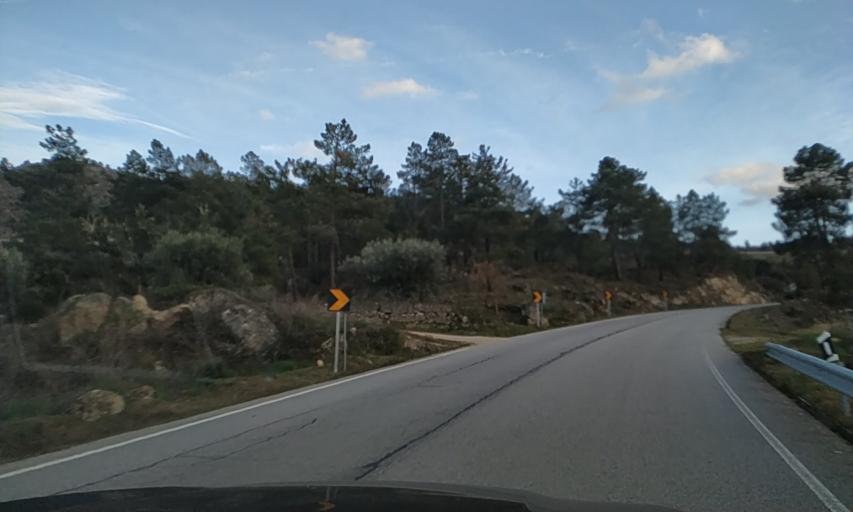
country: PT
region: Braganca
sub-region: Carrazeda de Ansiaes
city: Carrazeda de Anciaes
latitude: 41.2922
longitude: -7.3377
